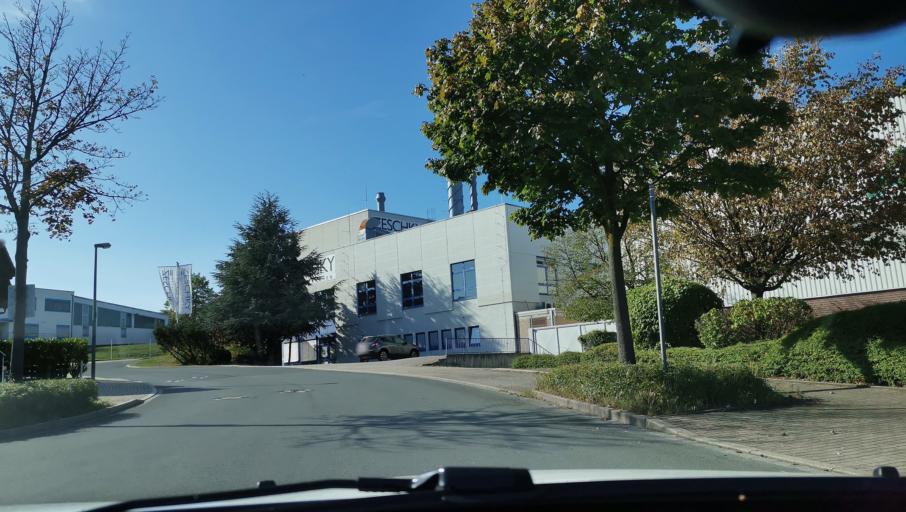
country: DE
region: North Rhine-Westphalia
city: Wetter (Ruhr)
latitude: 51.3583
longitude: 7.3804
